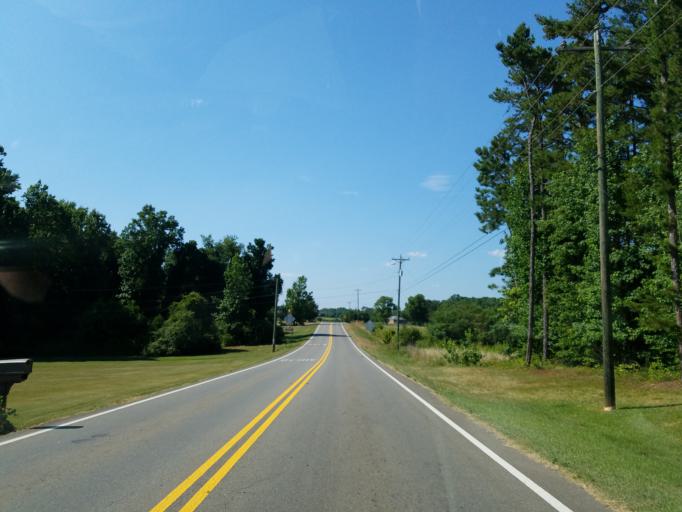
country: US
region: Georgia
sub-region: Fulton County
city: Milton
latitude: 34.2268
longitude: -84.2897
